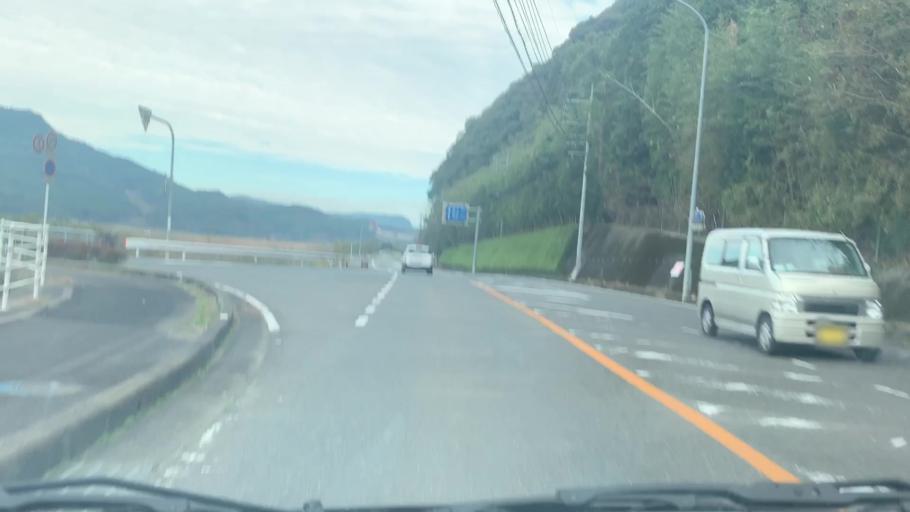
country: JP
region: Saga Prefecture
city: Imaricho-ko
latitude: 33.2709
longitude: 129.9647
